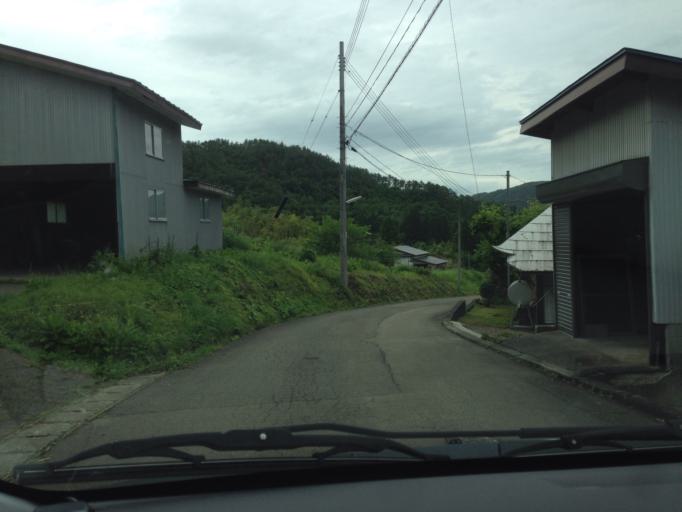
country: JP
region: Fukushima
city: Kitakata
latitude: 37.4018
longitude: 139.9093
